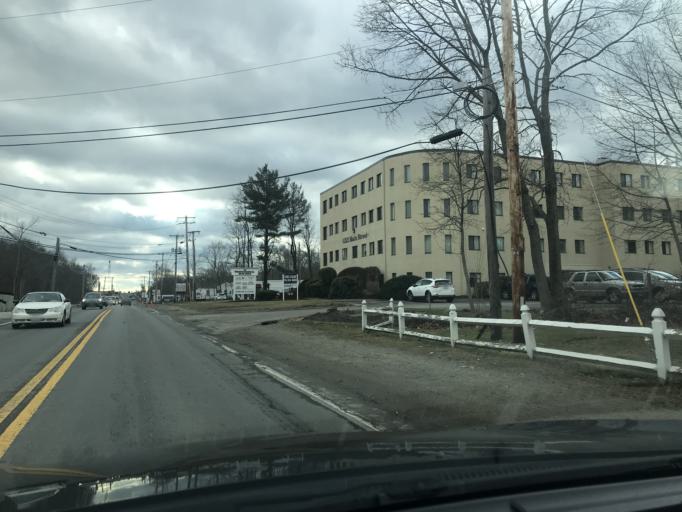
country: US
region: Massachusetts
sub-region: Plymouth County
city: Rockland
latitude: 42.1631
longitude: -70.9553
